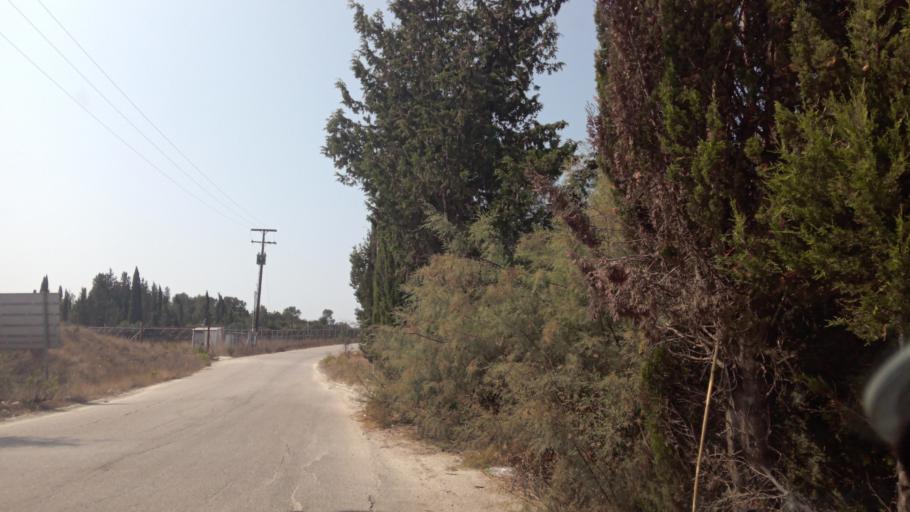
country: GR
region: Ionian Islands
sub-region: Nomos Kerkyras
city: Perivoli
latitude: 39.4185
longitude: 20.0325
